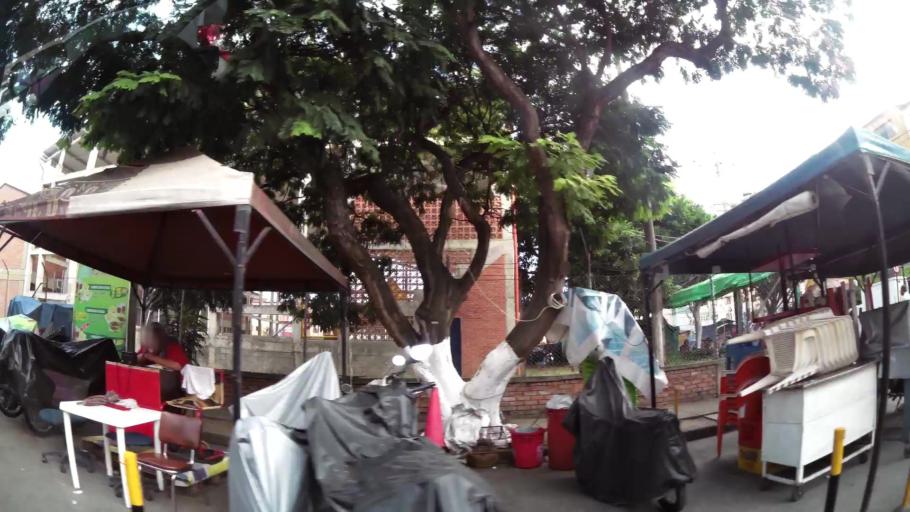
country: CO
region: Valle del Cauca
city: Cali
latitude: 3.4779
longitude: -76.4932
